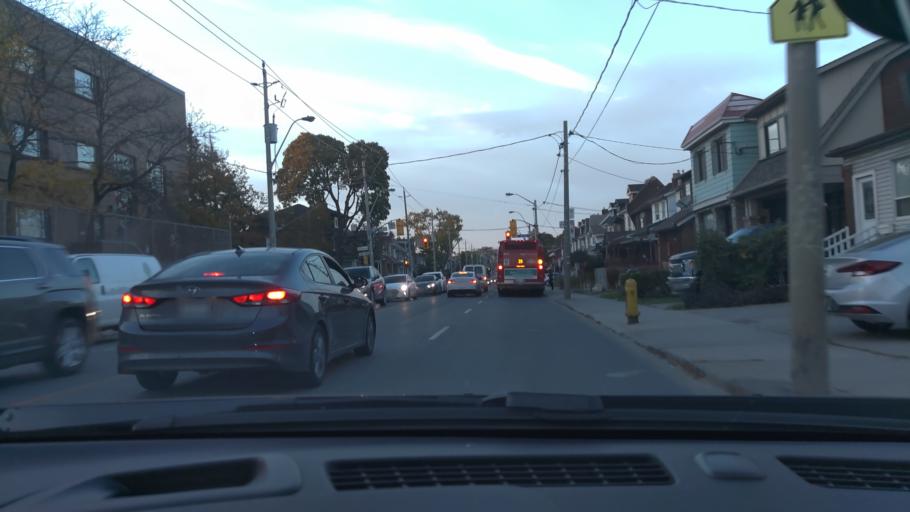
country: CA
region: Ontario
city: Toronto
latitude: 43.6796
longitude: -79.4436
